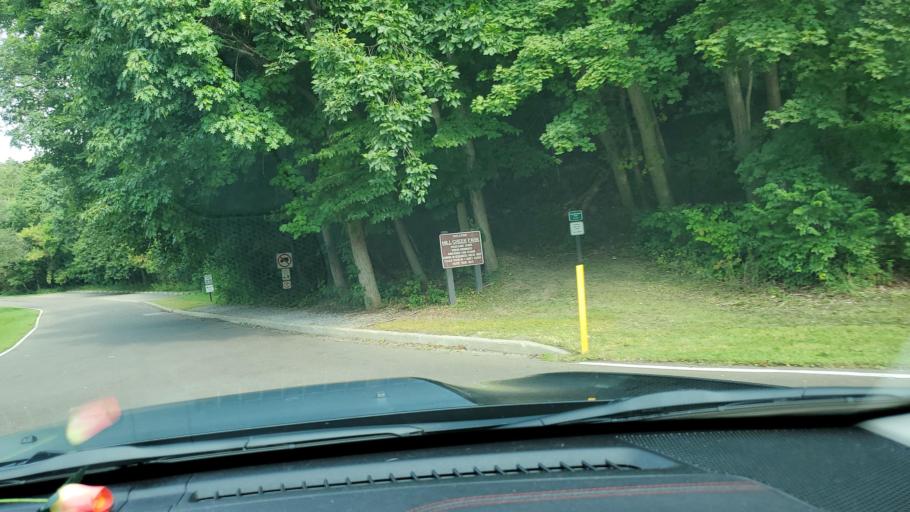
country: US
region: Ohio
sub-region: Mahoning County
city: Youngstown
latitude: 41.0975
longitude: -80.6783
